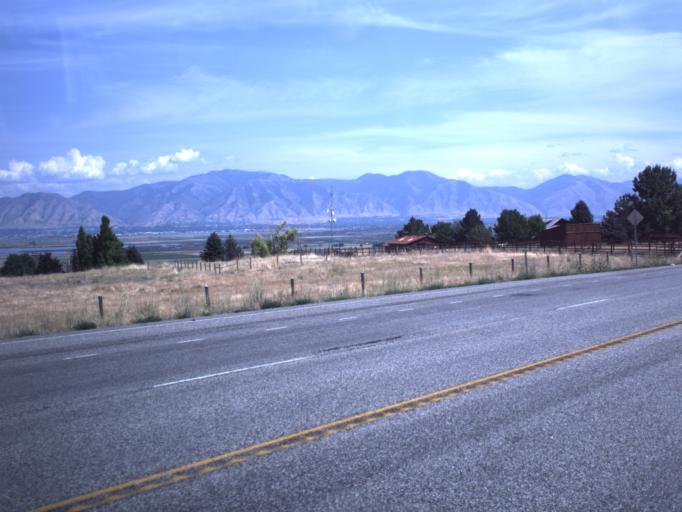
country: US
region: Utah
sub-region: Cache County
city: Mendon
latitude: 41.7625
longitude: -112.0086
